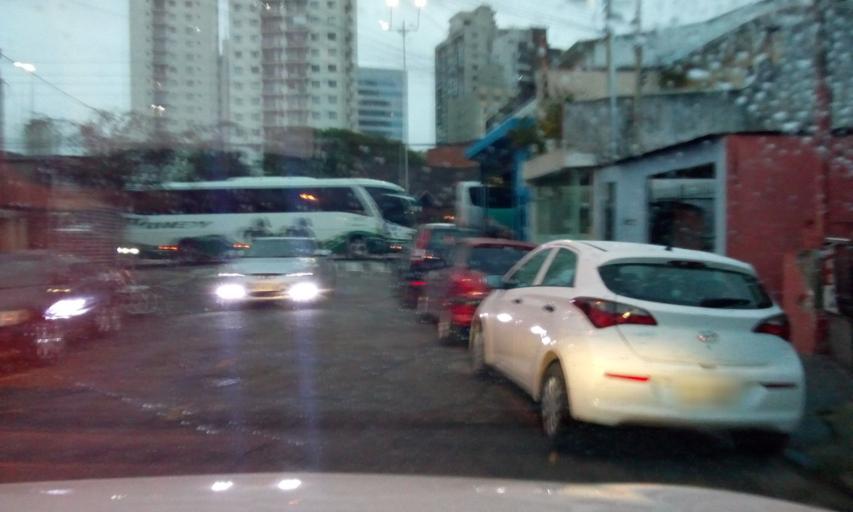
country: BR
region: Sao Paulo
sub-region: Sao Paulo
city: Sao Paulo
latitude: -23.6013
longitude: -46.6839
